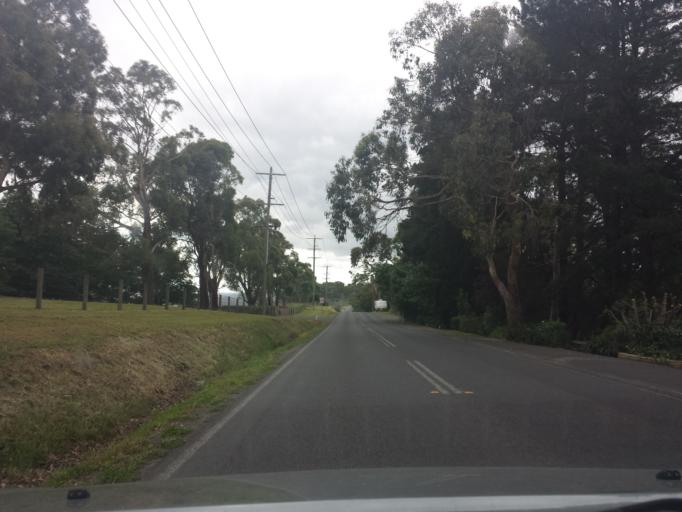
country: AU
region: Victoria
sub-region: Yarra Ranges
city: Belgrave South
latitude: -37.9173
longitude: 145.3210
